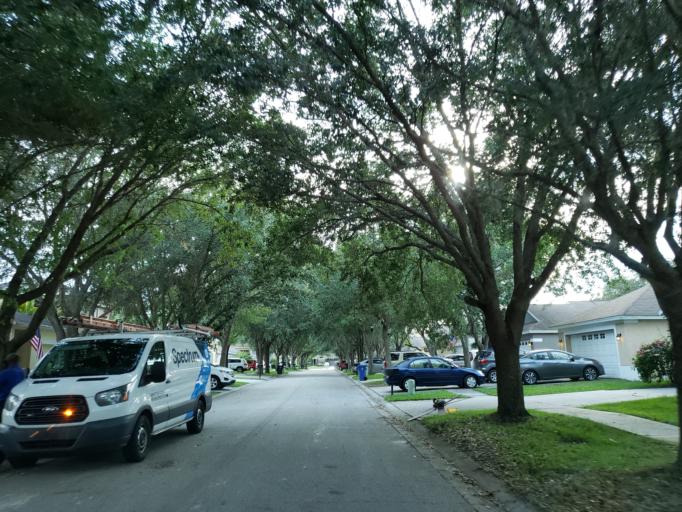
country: US
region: Florida
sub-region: Hillsborough County
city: Fish Hawk
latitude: 27.8461
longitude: -82.2278
